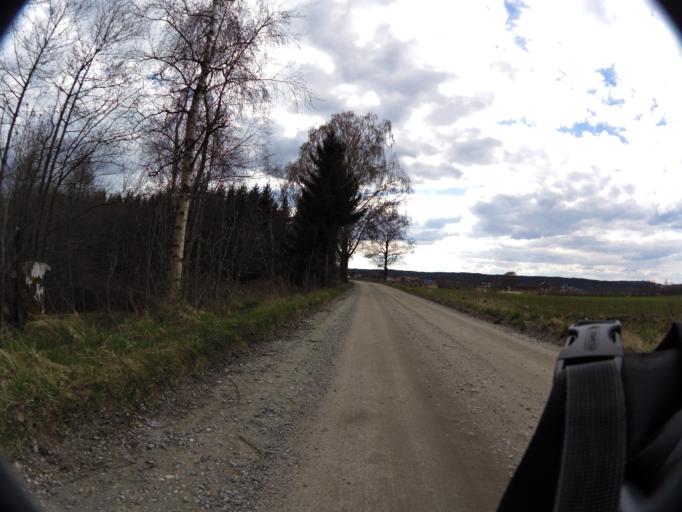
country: NO
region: Ostfold
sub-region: Sarpsborg
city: Sarpsborg
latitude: 59.2931
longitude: 11.0330
